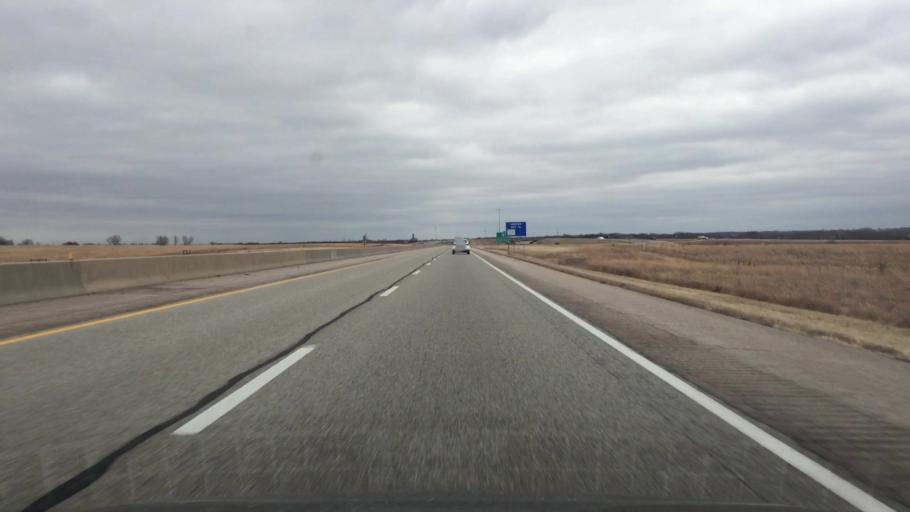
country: US
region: Kansas
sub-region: Butler County
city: El Dorado
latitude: 37.8840
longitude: -96.8412
